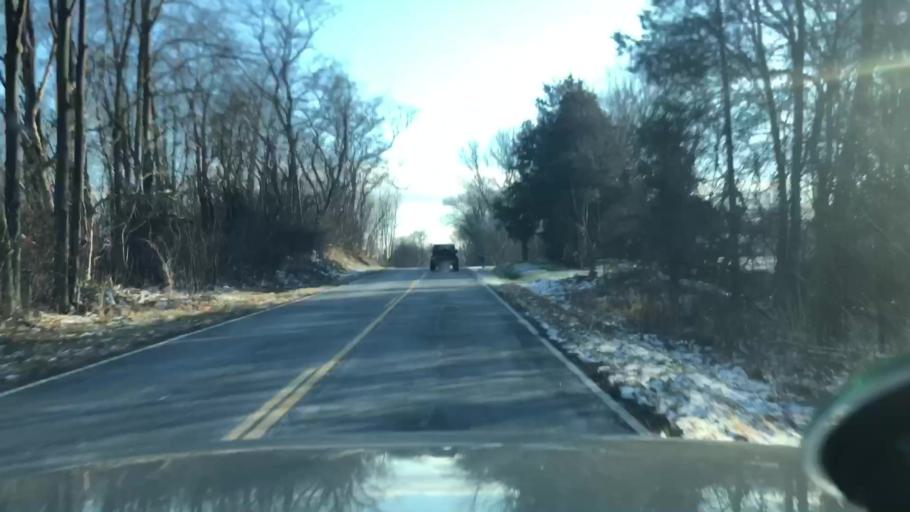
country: US
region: Michigan
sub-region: Jackson County
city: Vandercook Lake
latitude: 42.1272
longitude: -84.4515
